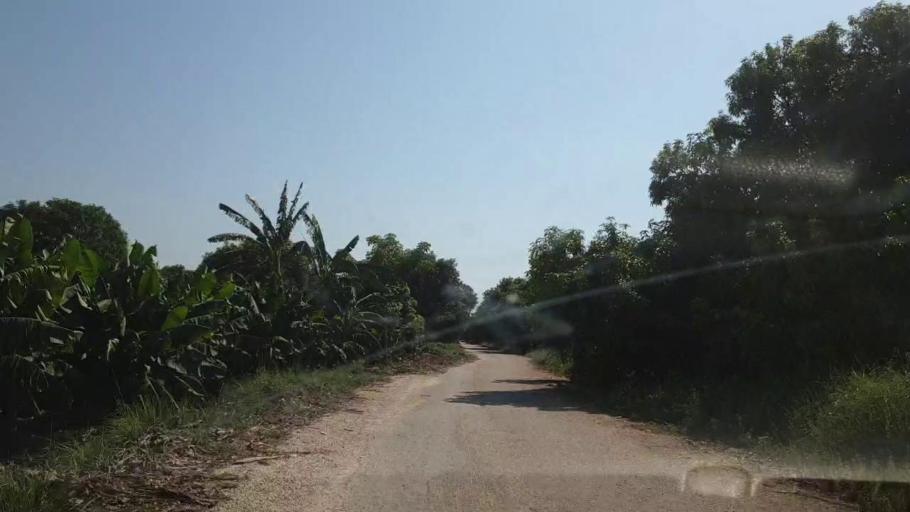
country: PK
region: Sindh
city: Tando Jam
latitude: 25.4098
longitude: 68.5821
